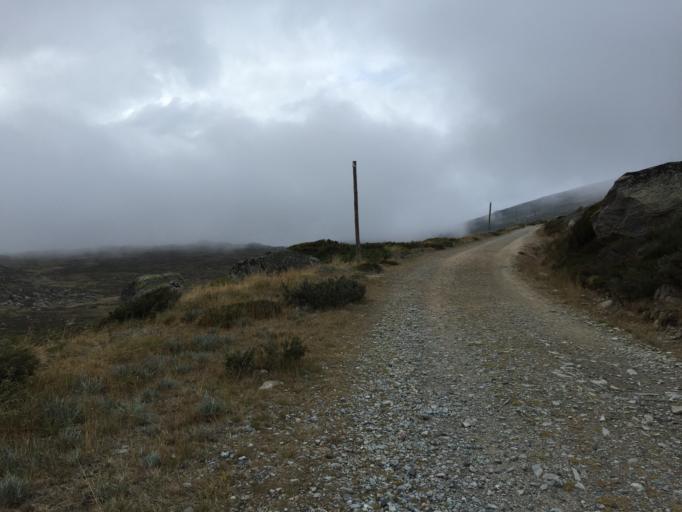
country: AU
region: New South Wales
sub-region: Snowy River
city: Jindabyne
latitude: -36.4555
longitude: 148.3020
